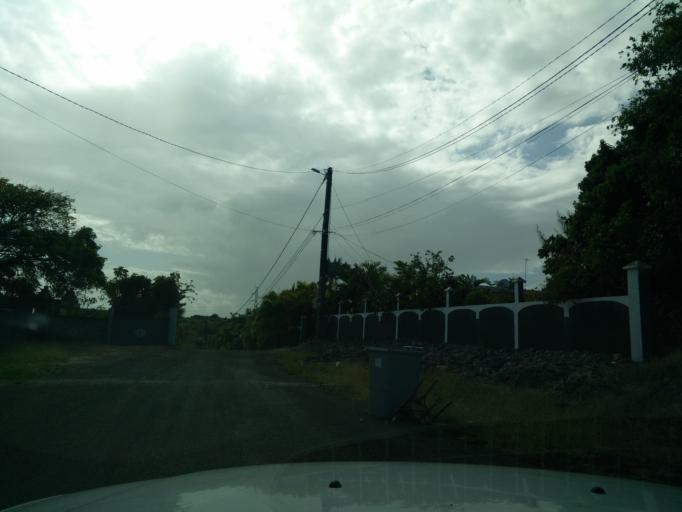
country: GP
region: Guadeloupe
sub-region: Guadeloupe
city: Sainte-Anne
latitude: 16.2332
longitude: -61.3819
